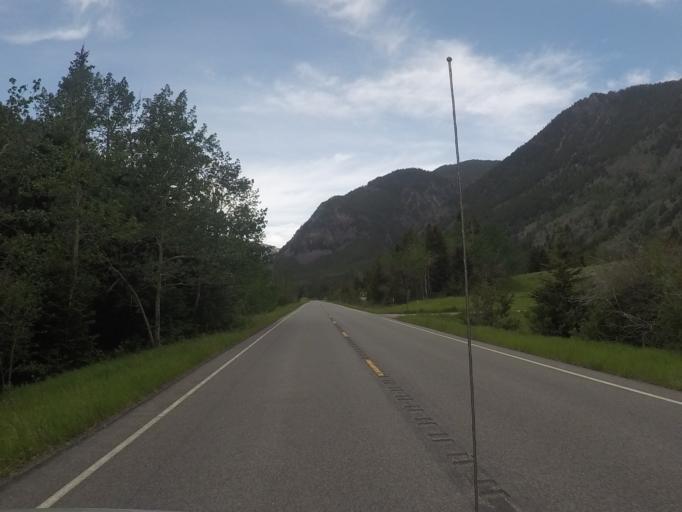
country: US
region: Montana
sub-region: Carbon County
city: Red Lodge
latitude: 45.0873
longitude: -109.3617
